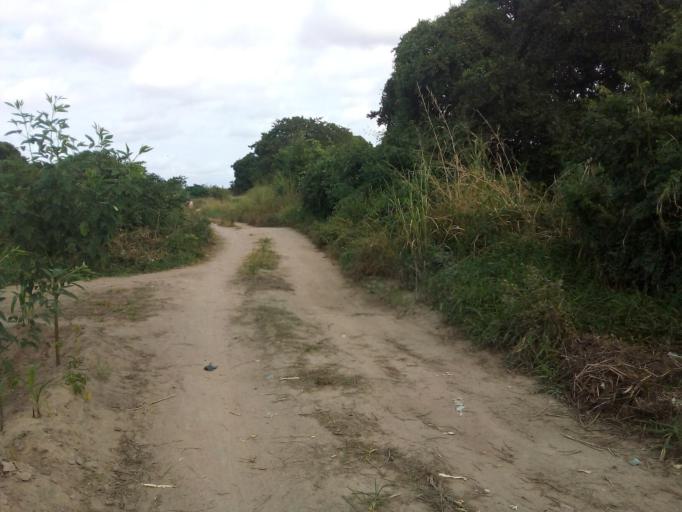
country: MZ
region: Zambezia
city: Quelimane
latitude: -17.5539
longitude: 36.6996
